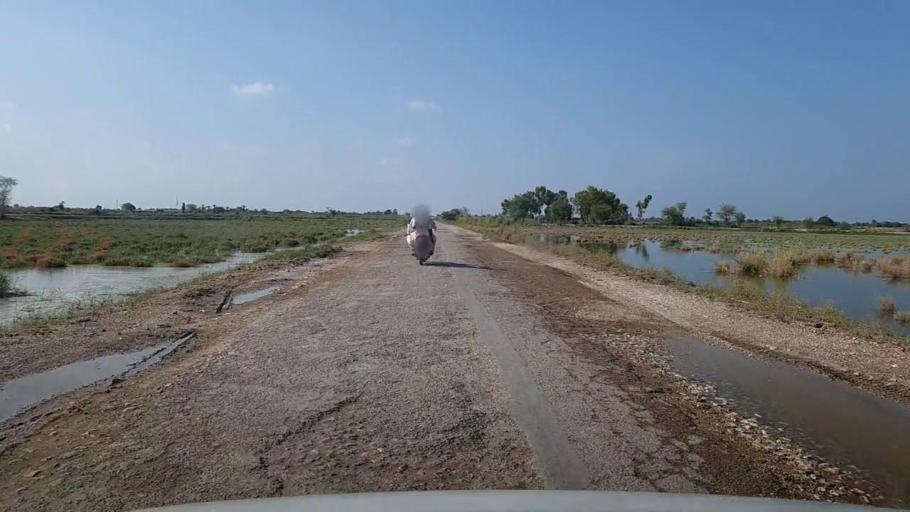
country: PK
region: Sindh
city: Kandiaro
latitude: 27.0628
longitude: 68.3158
